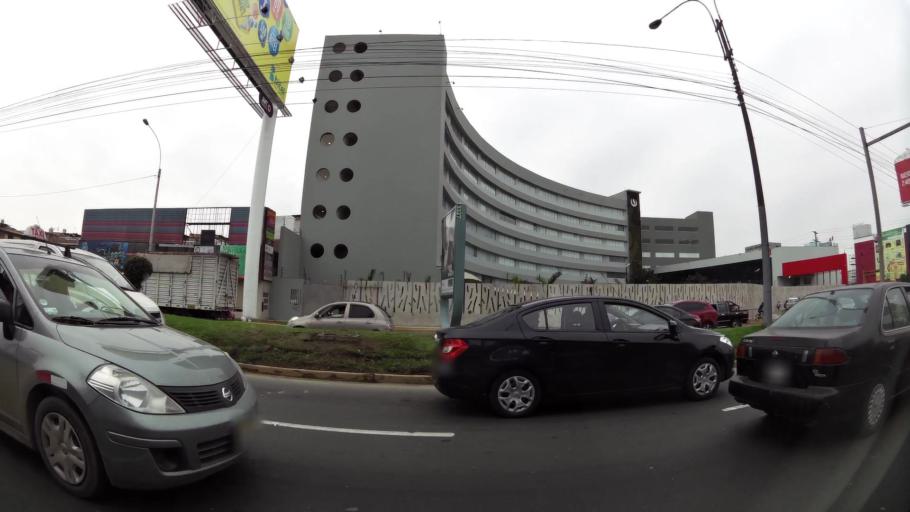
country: PE
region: Callao
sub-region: Callao
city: Callao
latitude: -12.0771
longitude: -77.0942
